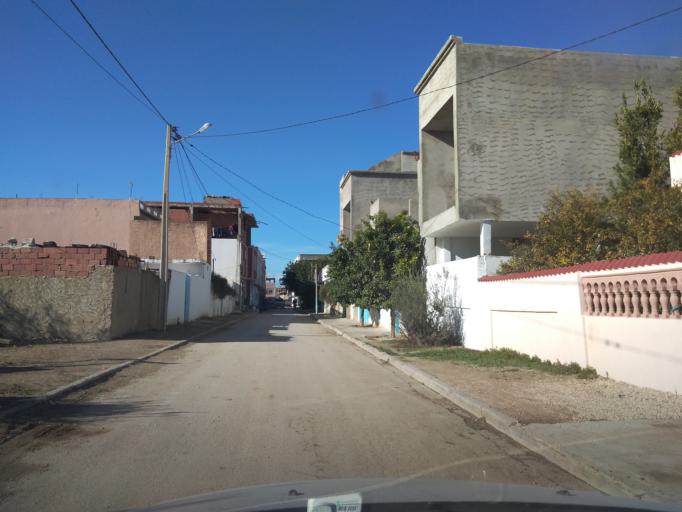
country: TN
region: Ariana
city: Qal'at al Andalus
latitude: 37.0653
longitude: 10.1228
